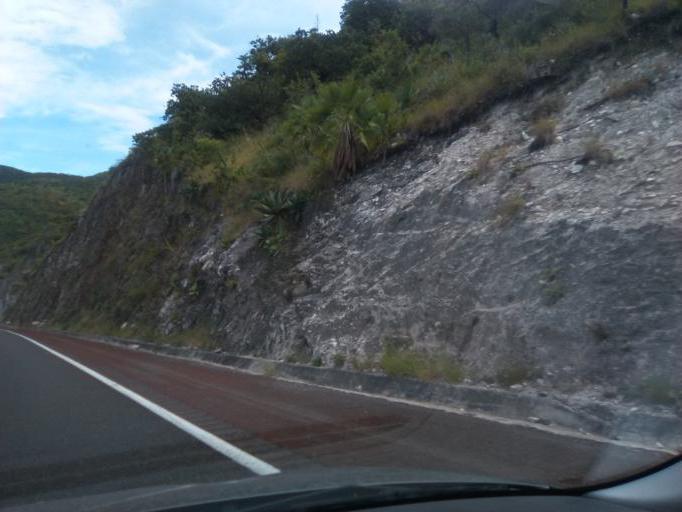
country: MX
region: Guerrero
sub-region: Eduardo Neri
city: Tlanipatla
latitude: 17.8512
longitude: -99.4136
